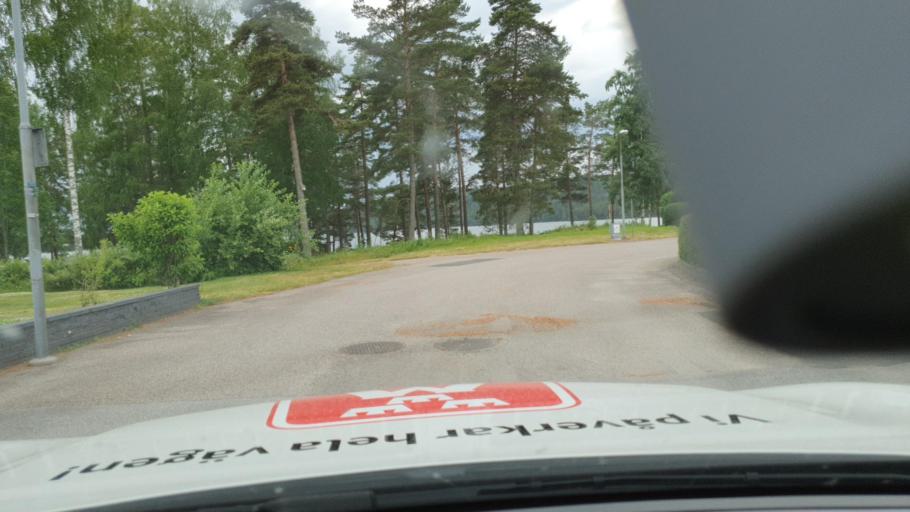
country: SE
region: Vaestra Goetaland
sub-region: Karlsborgs Kommun
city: Karlsborg
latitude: 58.5392
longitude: 14.4878
